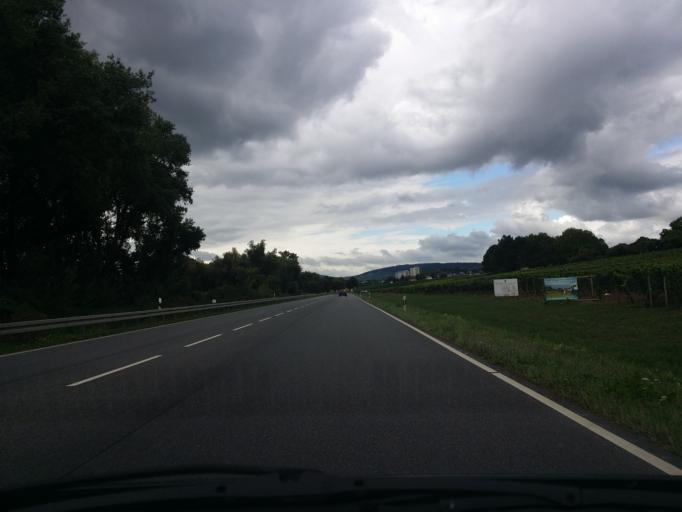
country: DE
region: Rheinland-Pfalz
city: Oestrich-Winkel
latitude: 49.9897
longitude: 7.9964
